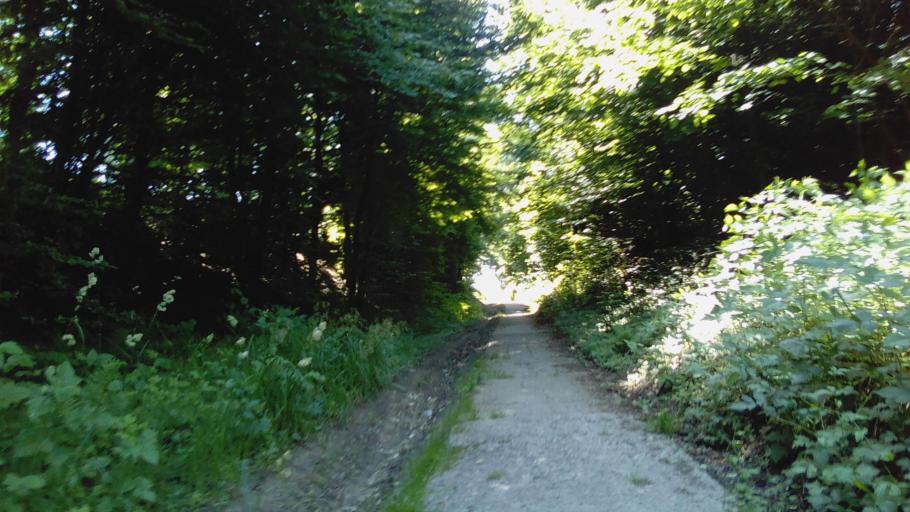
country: PL
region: Subcarpathian Voivodeship
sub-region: Powiat strzyzowski
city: Strzyzow
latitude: 49.8588
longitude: 21.7819
